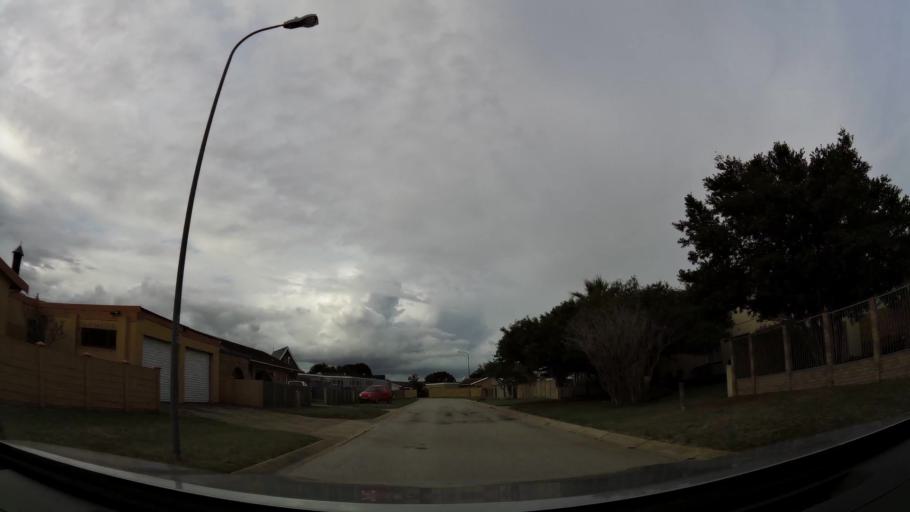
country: ZA
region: Eastern Cape
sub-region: Nelson Mandela Bay Metropolitan Municipality
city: Port Elizabeth
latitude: -33.9382
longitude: 25.4745
